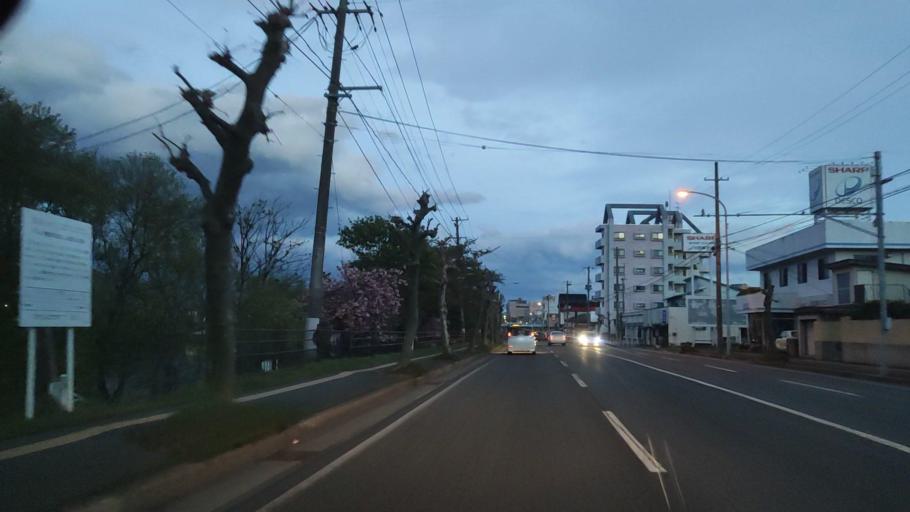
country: JP
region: Iwate
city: Morioka-shi
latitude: 39.7129
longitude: 141.1307
